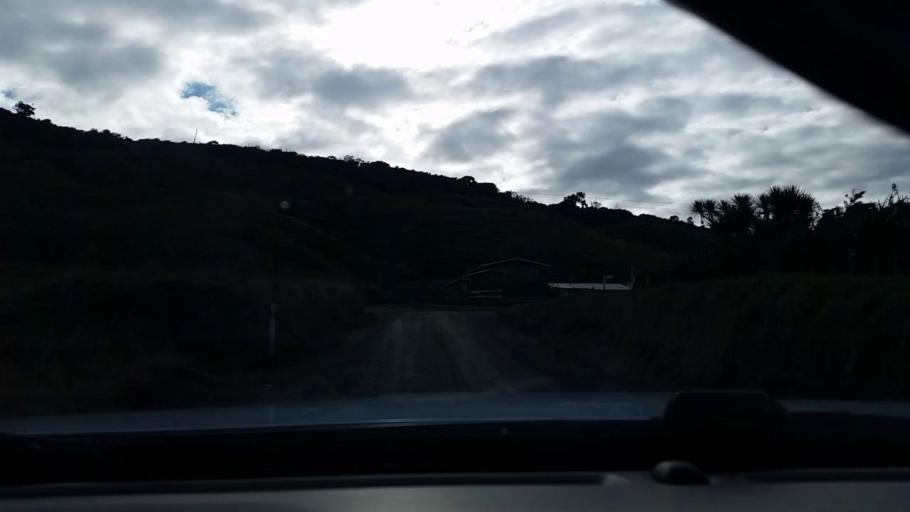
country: NZ
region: Southland
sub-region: Southland District
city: Riverton
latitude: -46.3308
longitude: 167.7125
